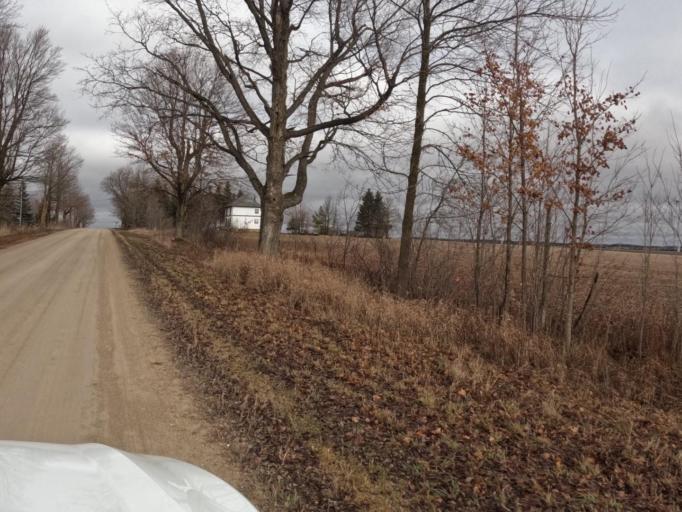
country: CA
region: Ontario
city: Shelburne
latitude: 43.9960
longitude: -80.4085
